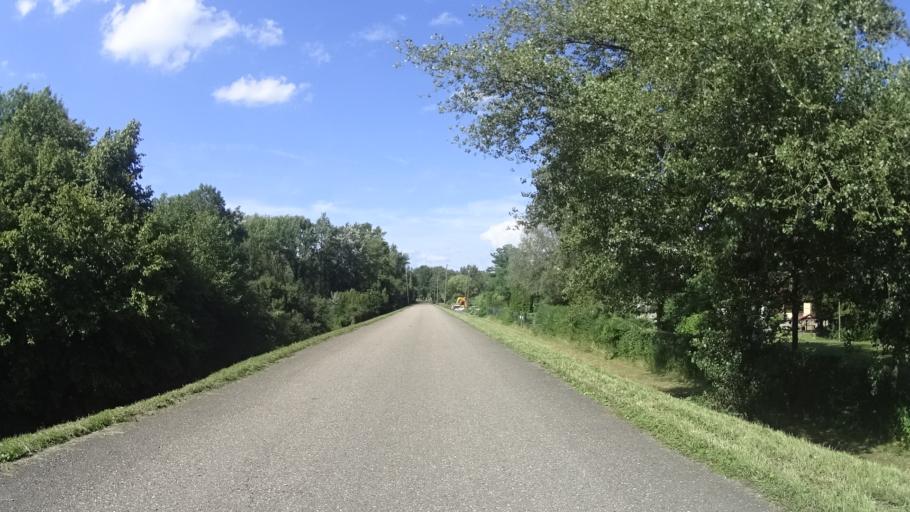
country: DE
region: Baden-Wuerttemberg
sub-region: Karlsruhe Region
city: Iffezheim
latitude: 48.8448
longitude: 8.1073
